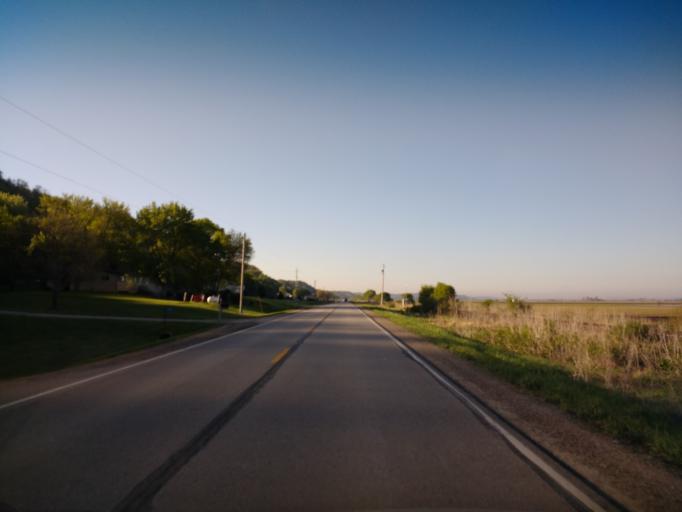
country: US
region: Iowa
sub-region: Harrison County
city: Missouri Valley
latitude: 41.4780
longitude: -95.8830
